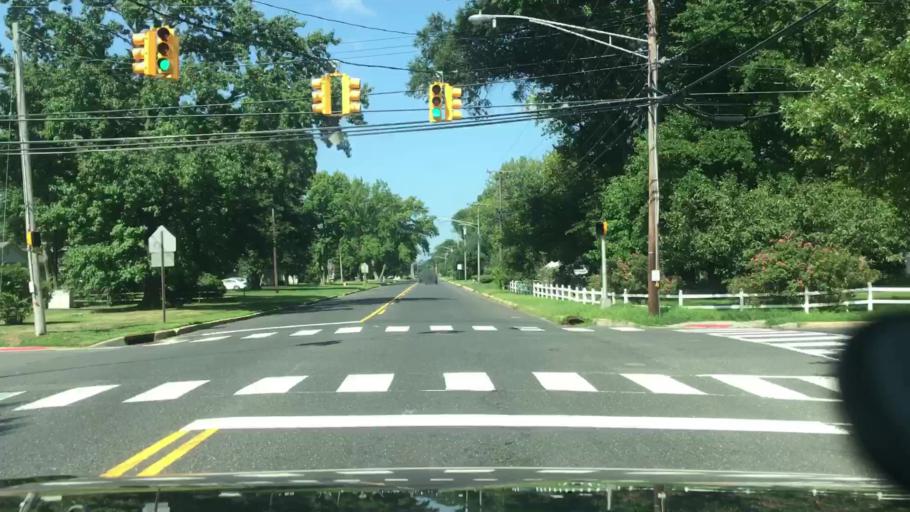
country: US
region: New Jersey
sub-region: Monmouth County
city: Oceanport
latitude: 40.3213
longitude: -74.0049
